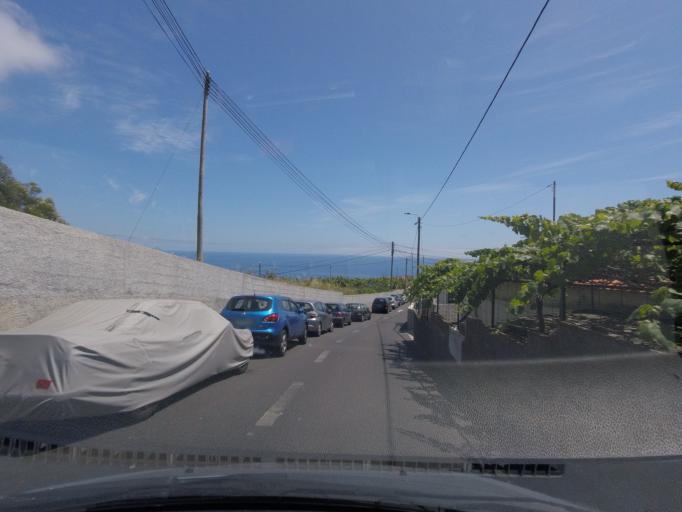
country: PT
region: Madeira
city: Camara de Lobos
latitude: 32.6508
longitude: -16.9500
